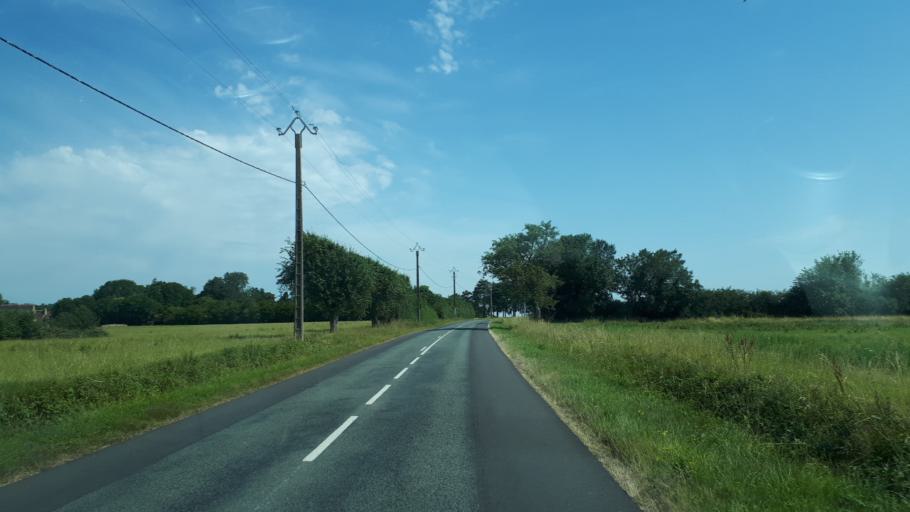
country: FR
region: Centre
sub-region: Departement du Loir-et-Cher
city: Aze
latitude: 47.8683
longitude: 1.0027
